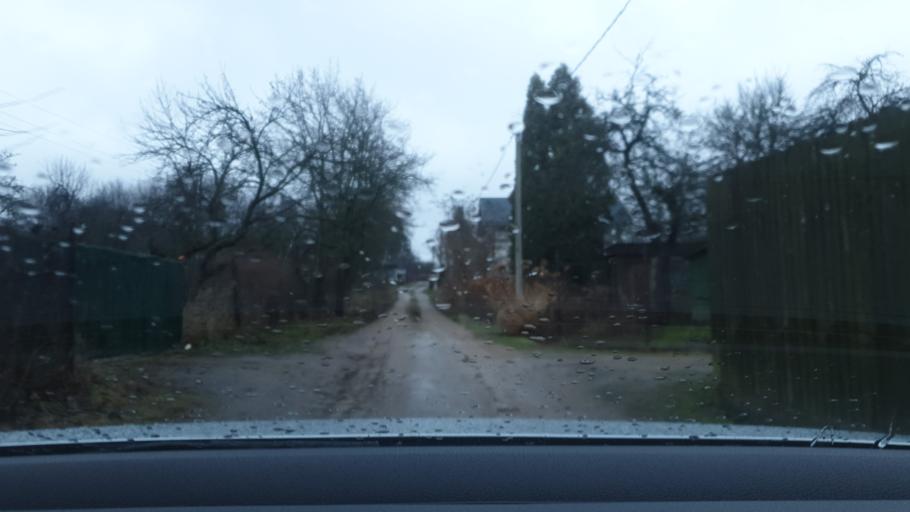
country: LT
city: Skaidiskes
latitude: 54.7037
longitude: 25.4036
